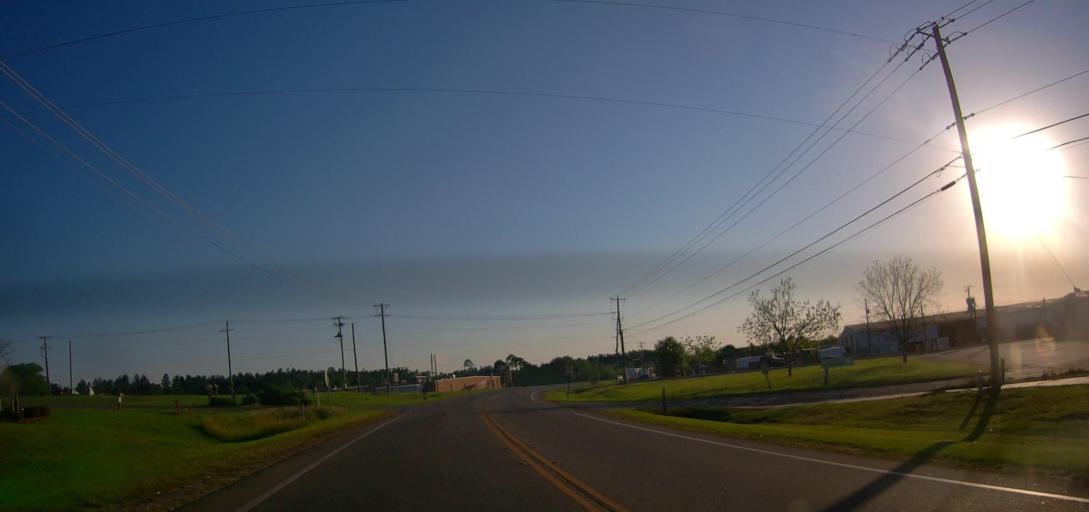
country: US
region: Georgia
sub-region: Ben Hill County
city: Fitzgerald
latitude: 31.6953
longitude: -83.2401
